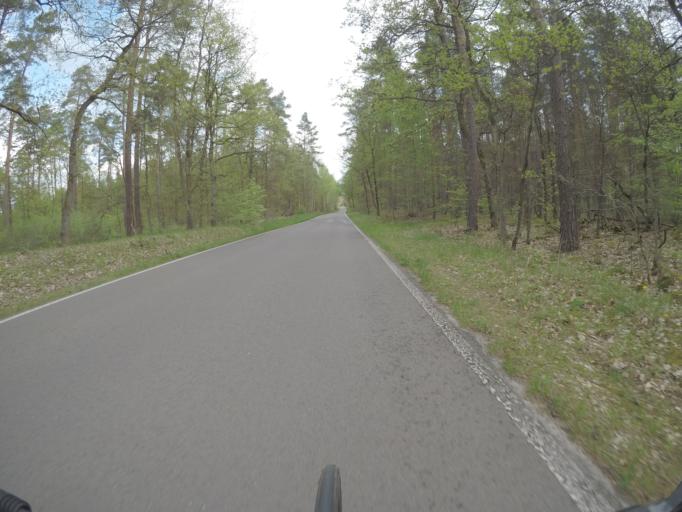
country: DE
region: Brandenburg
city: Marienwerder
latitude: 52.8771
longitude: 13.6316
